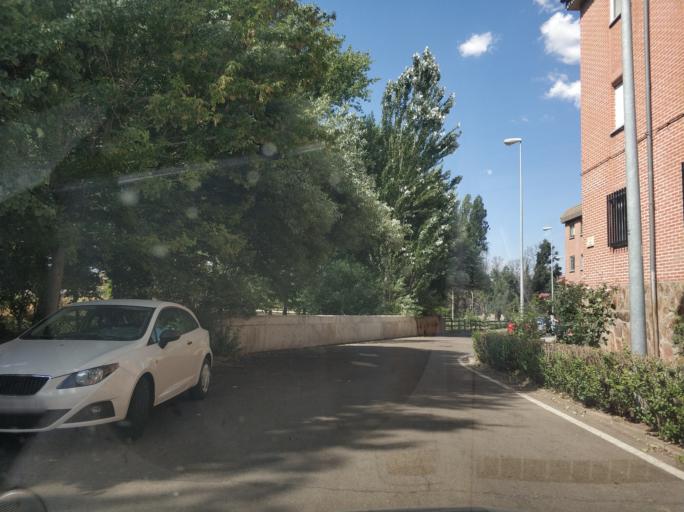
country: ES
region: Castille and Leon
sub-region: Provincia de Salamanca
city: Aldeatejada
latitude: 40.9544
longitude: -5.7002
